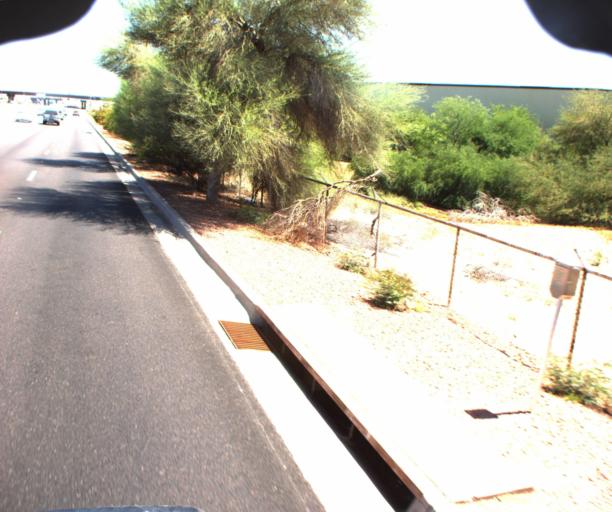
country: US
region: Arizona
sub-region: Maricopa County
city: Peoria
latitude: 33.5699
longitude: -112.2241
